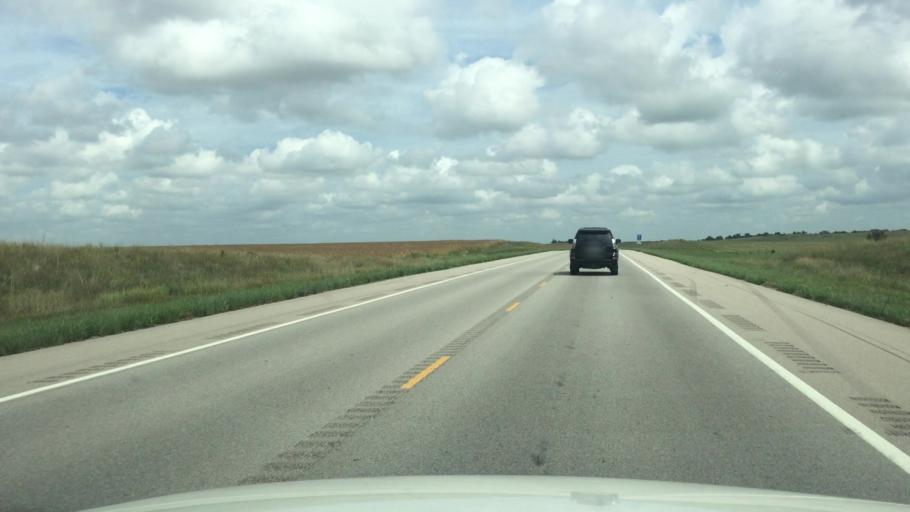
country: US
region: Kansas
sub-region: Allen County
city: Iola
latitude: 38.0482
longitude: -95.3810
